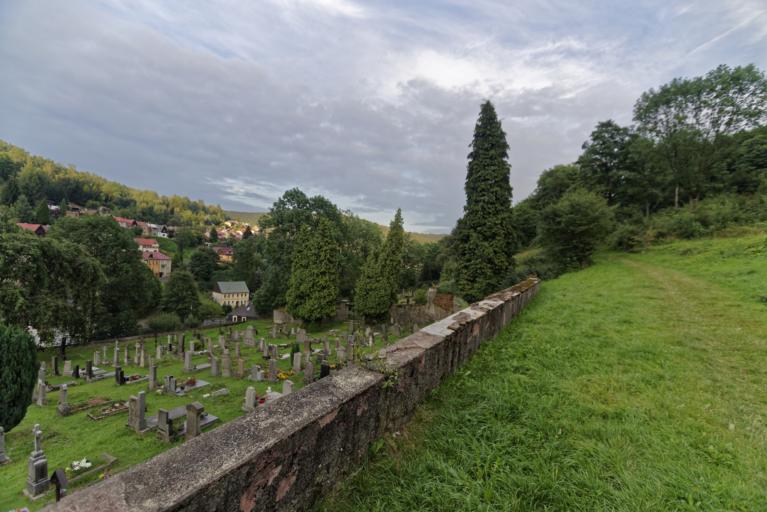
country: CZ
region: Karlovarsky
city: Jachymov
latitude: 50.3636
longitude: 12.9229
